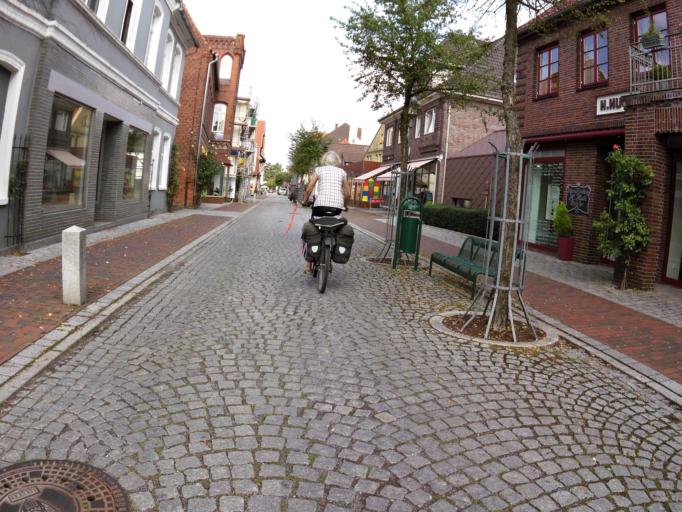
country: DE
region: Lower Saxony
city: Hoya
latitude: 52.8062
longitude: 9.1439
